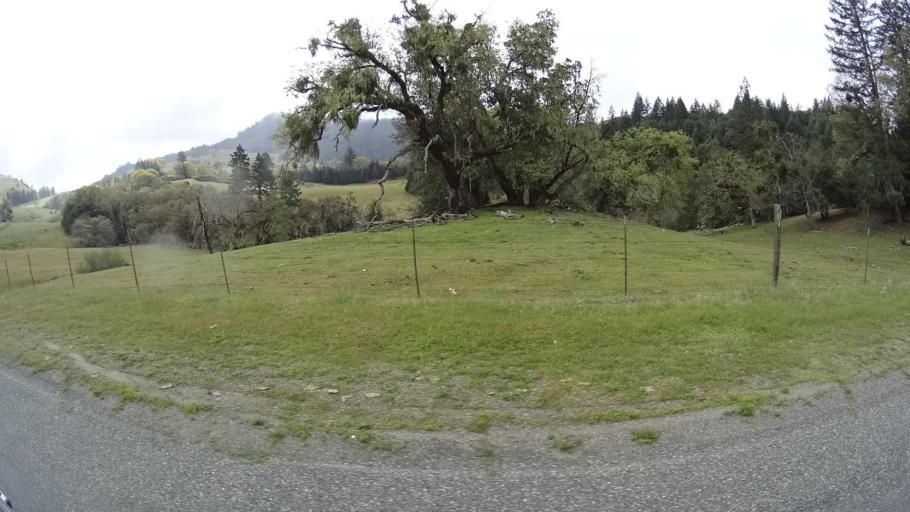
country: US
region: California
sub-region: Humboldt County
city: Redway
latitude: 40.1567
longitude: -123.5470
